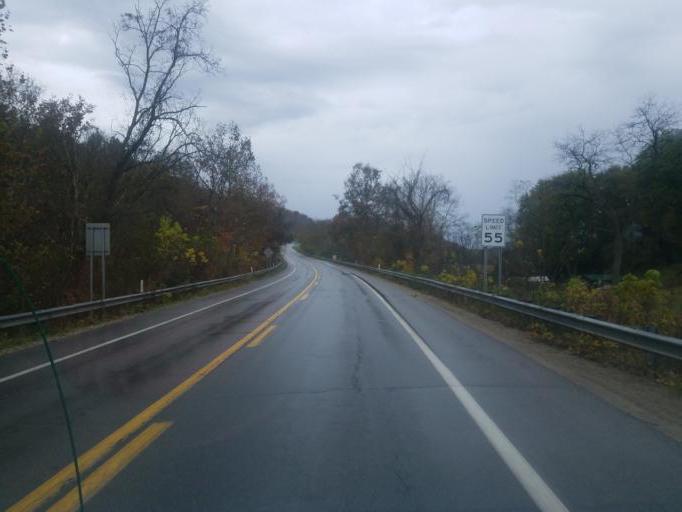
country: US
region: West Virginia
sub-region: Wood County
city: Boaz
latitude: 39.3604
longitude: -81.5016
